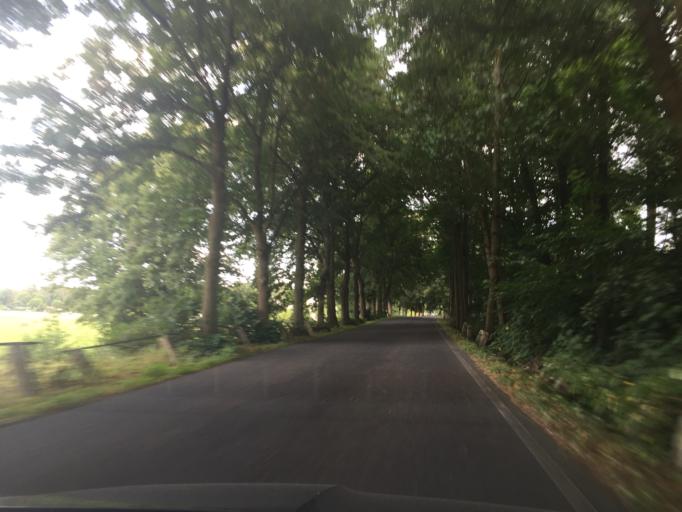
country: DE
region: Brandenburg
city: Spreenhagen
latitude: 52.3436
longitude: 13.8464
